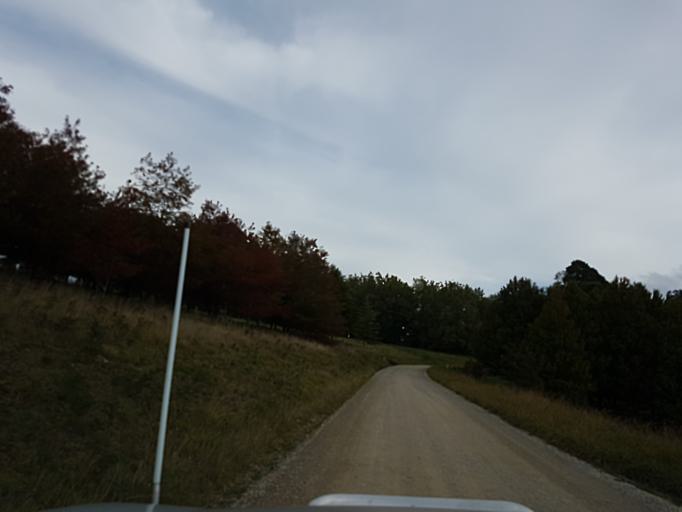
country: AU
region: Victoria
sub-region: Yarra Ranges
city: Olinda
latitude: -37.8587
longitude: 145.3870
